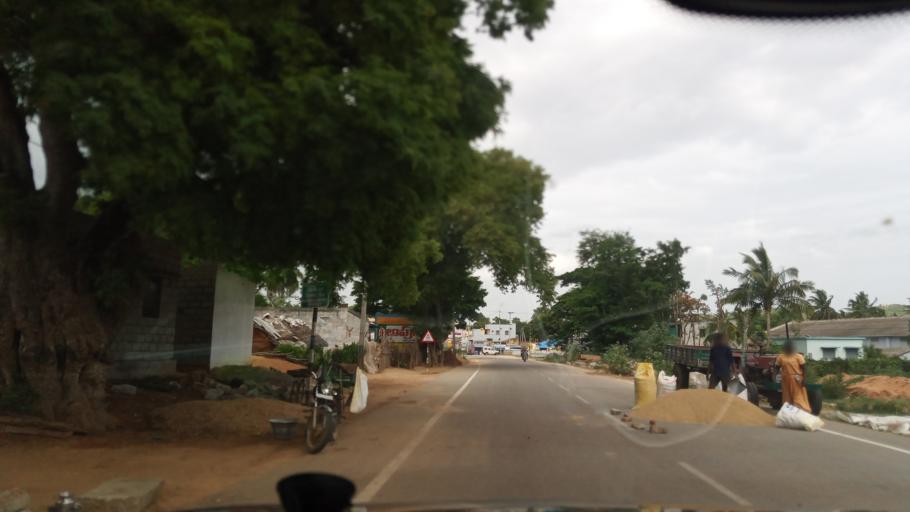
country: IN
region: Andhra Pradesh
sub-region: Chittoor
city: Palmaner
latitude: 13.1855
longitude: 78.8347
